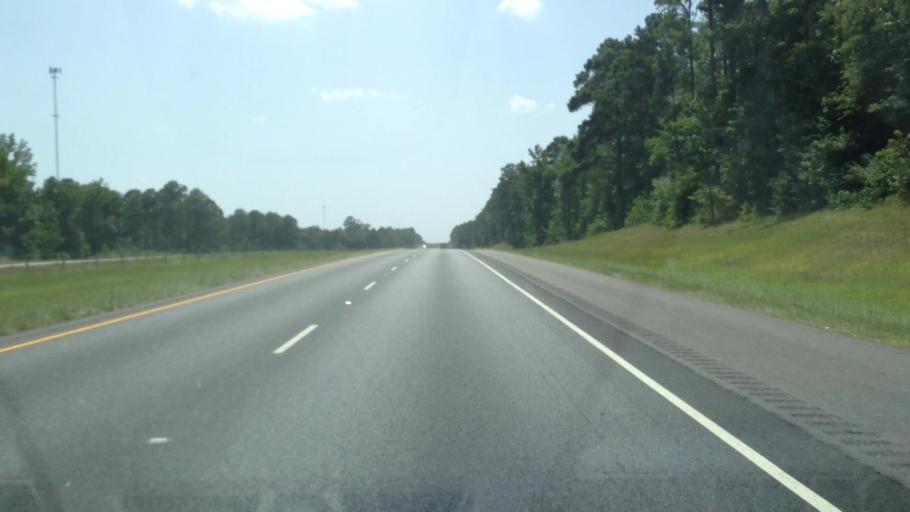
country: US
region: Louisiana
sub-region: Webster Parish
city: Minden
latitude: 32.5629
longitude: -93.1087
